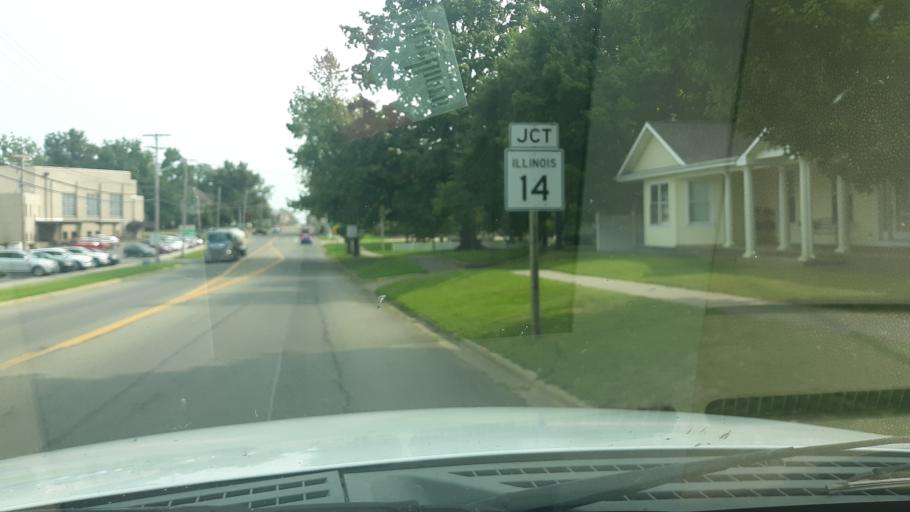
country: US
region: Illinois
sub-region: White County
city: Carmi
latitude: 38.0863
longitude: -88.1662
